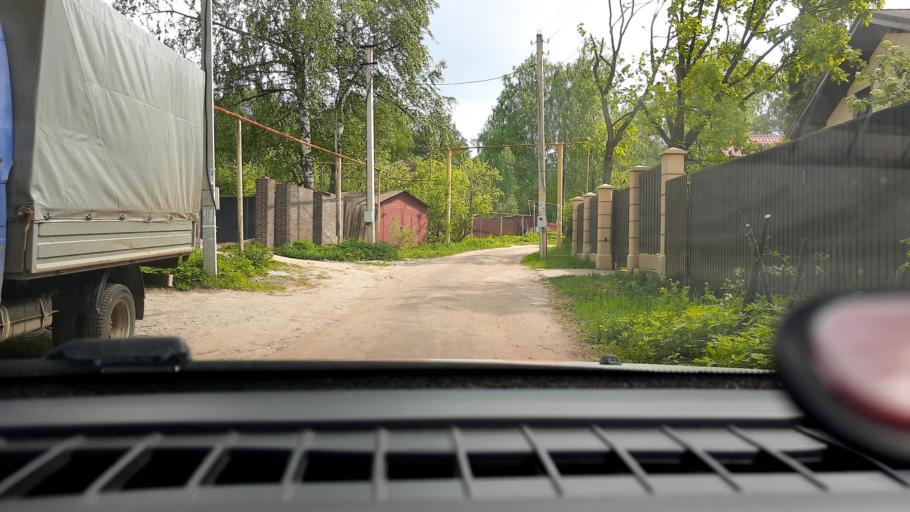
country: RU
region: Nizjnij Novgorod
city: Afonino
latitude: 56.1876
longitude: 44.0992
